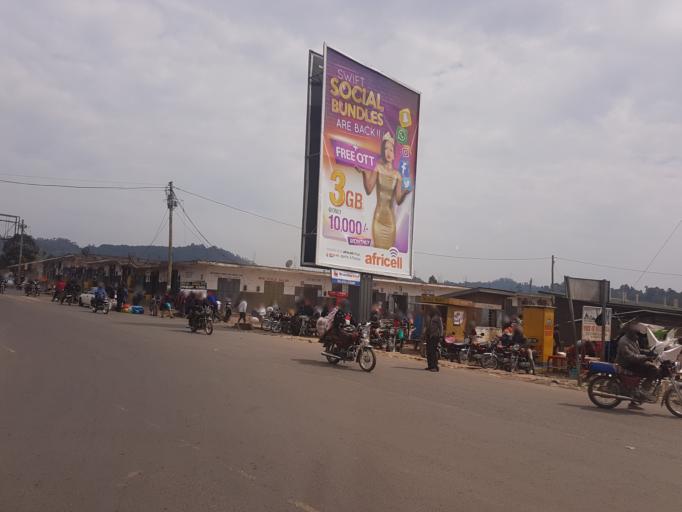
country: UG
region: Western Region
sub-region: Kisoro District
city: Kisoro
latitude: -1.2829
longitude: 29.7013
